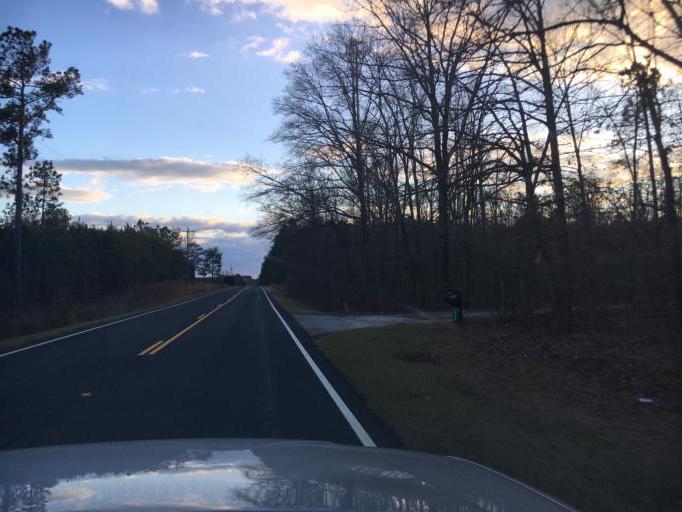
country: US
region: South Carolina
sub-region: Greenwood County
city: Greenwood
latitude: 34.0678
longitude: -82.2273
